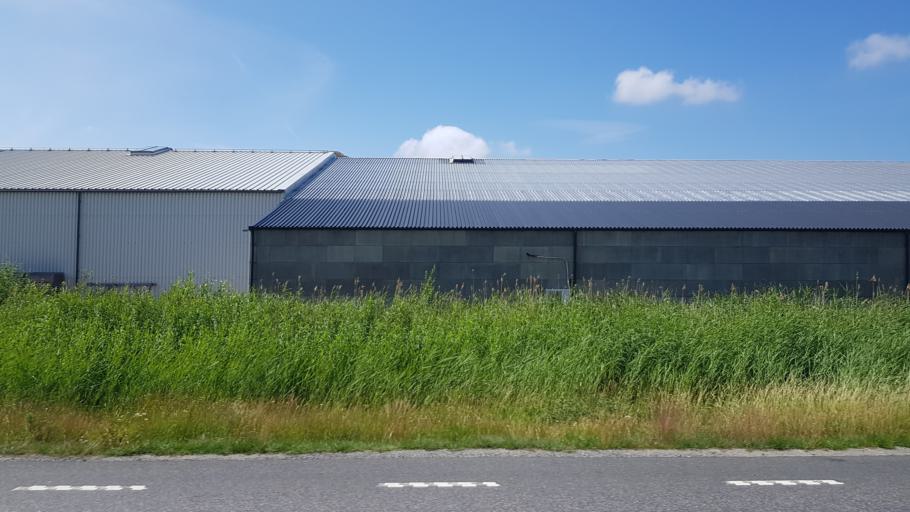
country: SE
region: Vaestra Goetaland
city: Ronnang
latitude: 57.9484
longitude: 11.5698
